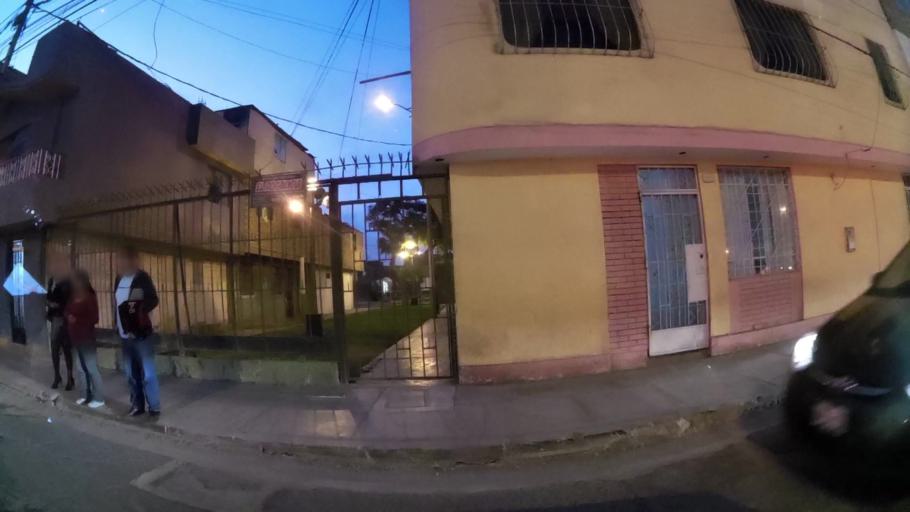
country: PE
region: Callao
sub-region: Callao
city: Callao
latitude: -12.0539
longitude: -77.1011
